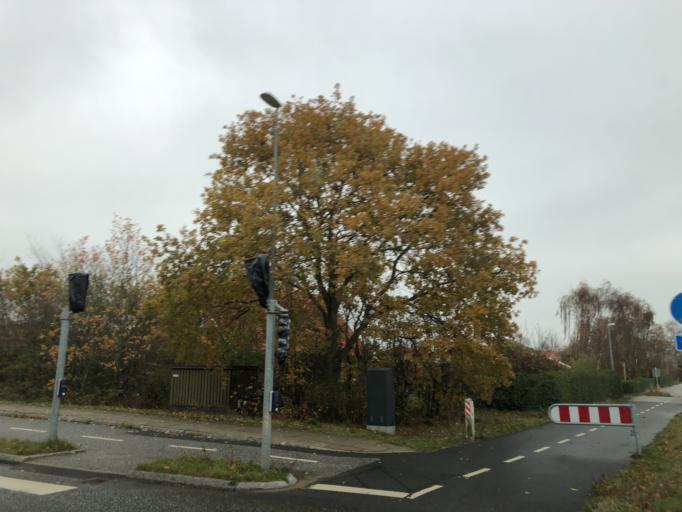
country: DK
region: Central Jutland
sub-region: Herning Kommune
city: Sunds
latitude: 56.2054
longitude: 8.9953
